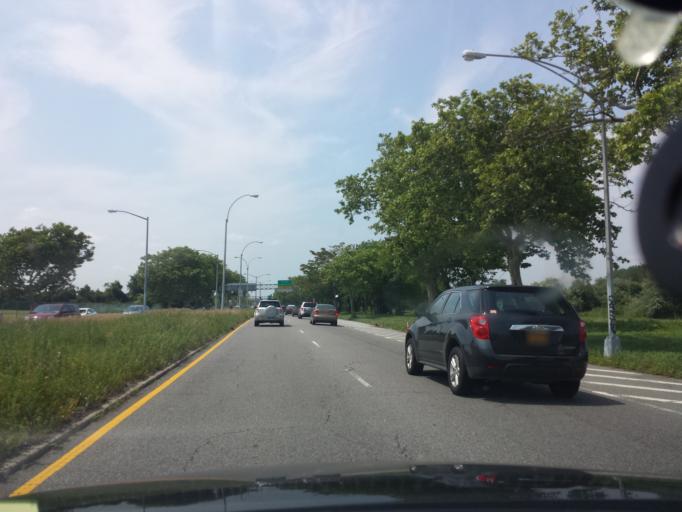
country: US
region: New York
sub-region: Kings County
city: Brooklyn
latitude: 40.5914
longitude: -73.9022
